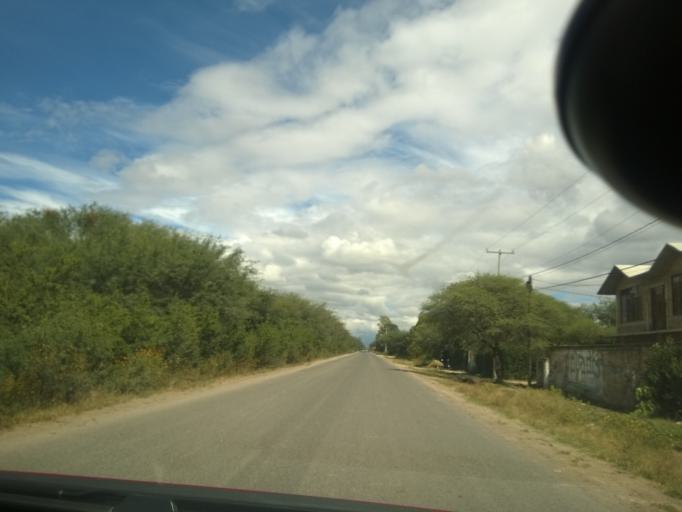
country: MX
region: Guanajuato
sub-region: Leon
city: Plan Guanajuato (La Sandia)
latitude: 20.9620
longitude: -101.6394
